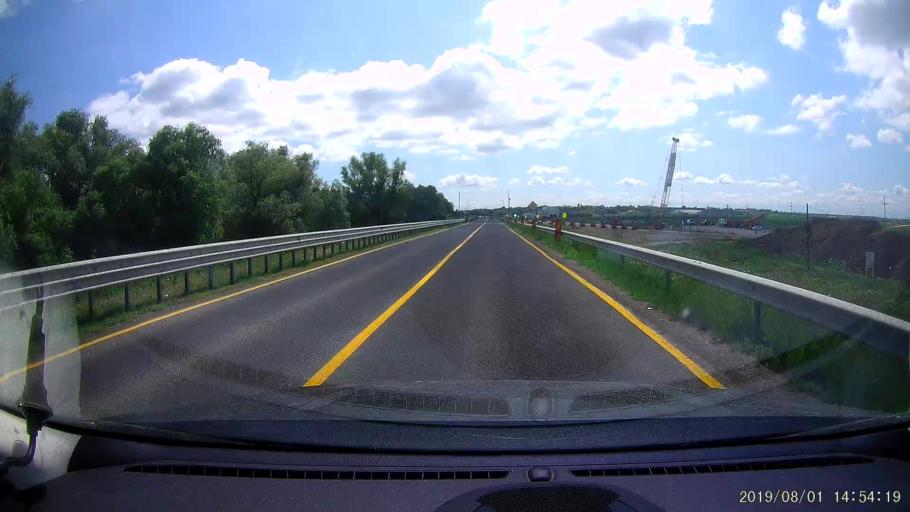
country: RO
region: Braila
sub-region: Municipiul Braila
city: Braila
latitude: 45.3198
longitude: 27.9908
